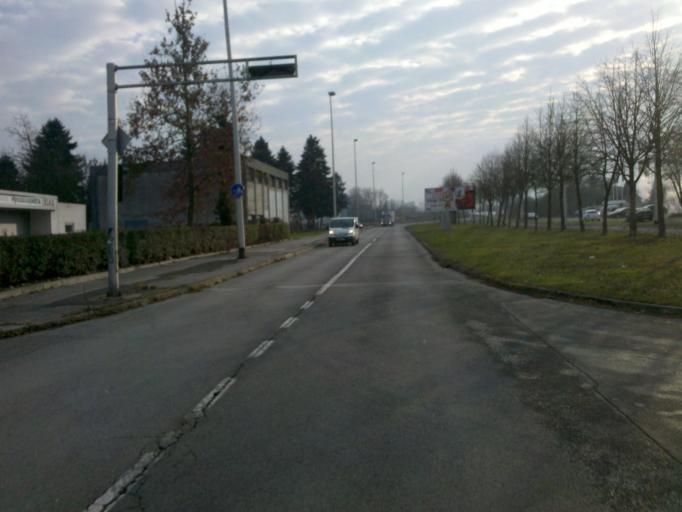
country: HR
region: Grad Zagreb
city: Dubrava
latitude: 45.7955
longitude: 16.0386
